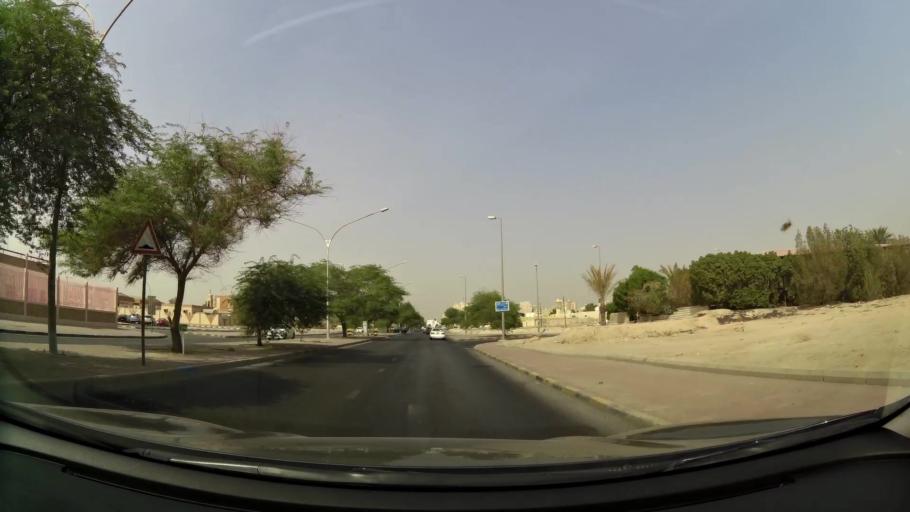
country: KW
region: Al Farwaniyah
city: Al Farwaniyah
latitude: 29.2480
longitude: 47.9326
